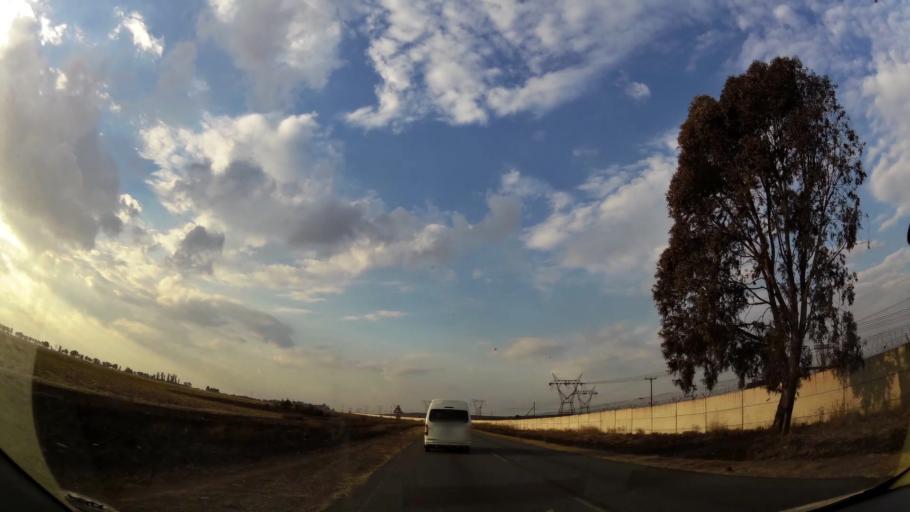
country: ZA
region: Gauteng
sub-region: Sedibeng District Municipality
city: Vanderbijlpark
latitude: -26.6572
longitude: 27.8013
